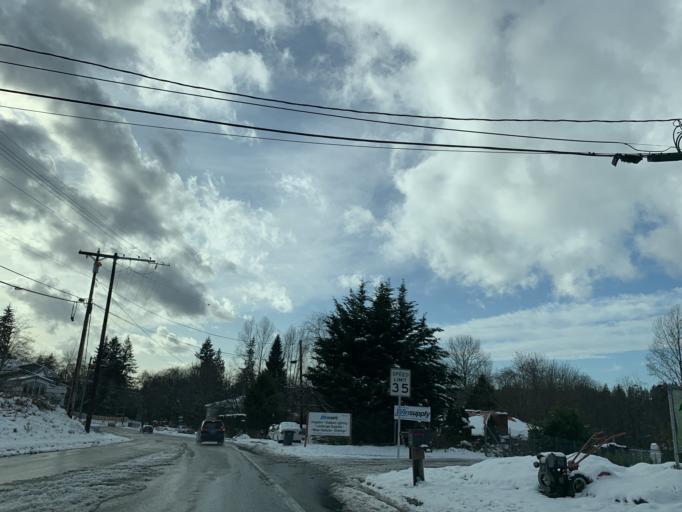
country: US
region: Washington
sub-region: Snohomish County
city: Martha Lake
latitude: 47.8489
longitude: -122.2615
